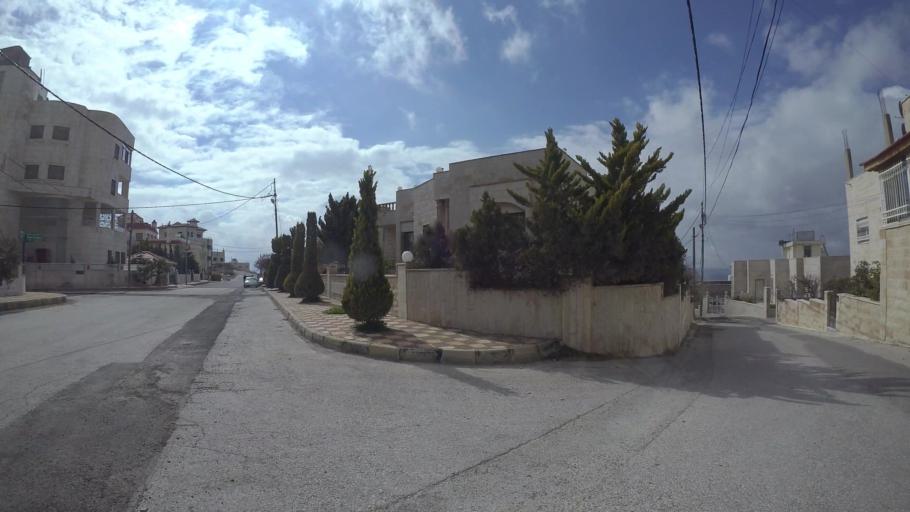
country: JO
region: Amman
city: Al Jubayhah
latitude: 32.0714
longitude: 35.8804
